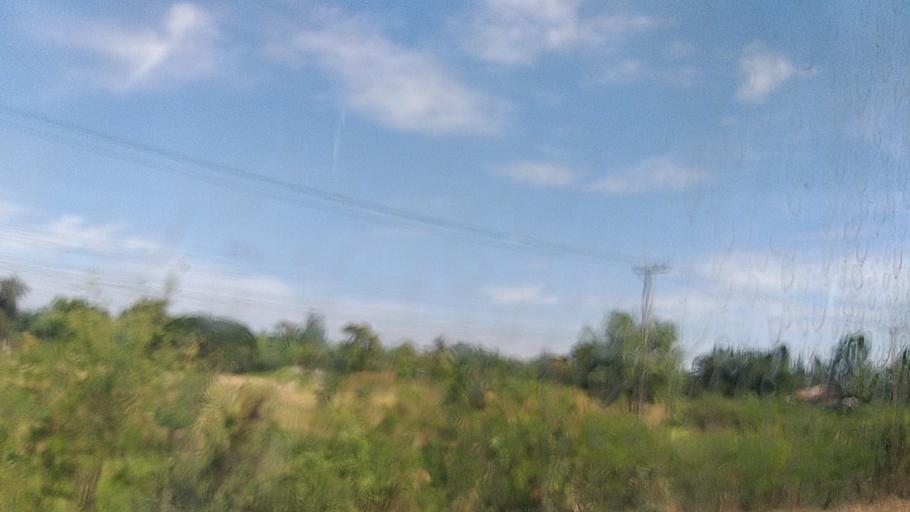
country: TH
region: Khon Kaen
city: Khon Kaen
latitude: 16.4088
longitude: 102.8939
